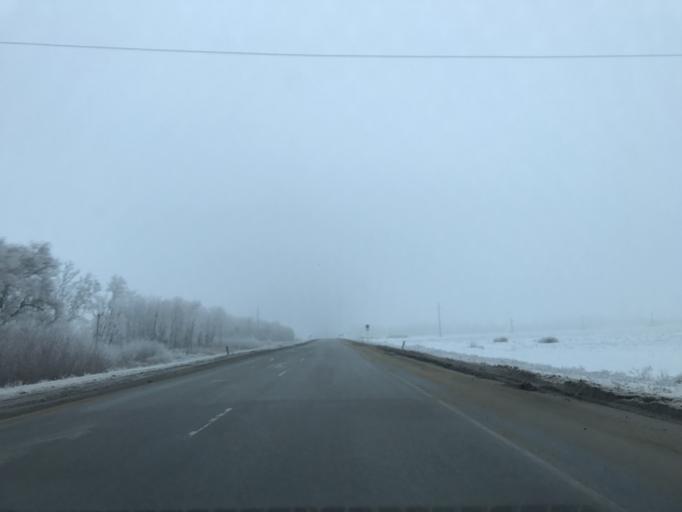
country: RU
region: Rostov
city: Temernik
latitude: 47.3782
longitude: 39.8249
